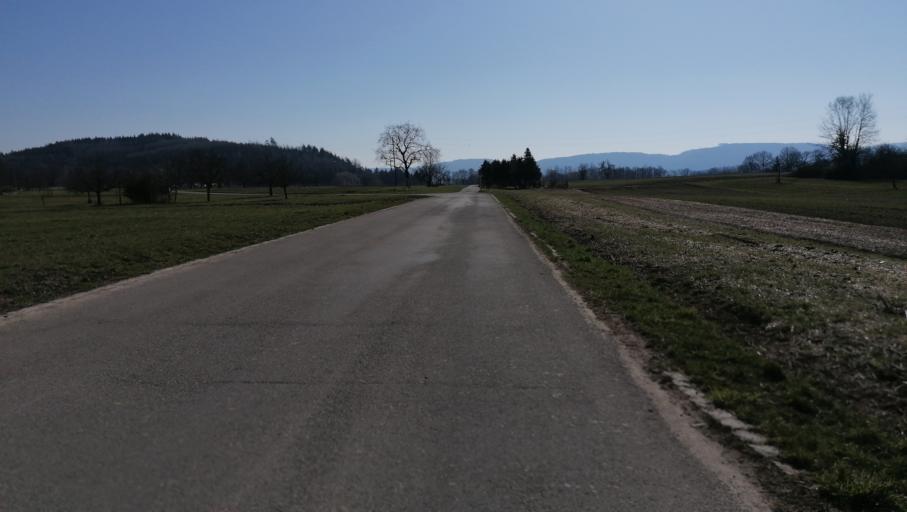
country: DE
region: Baden-Wuerttemberg
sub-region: Freiburg Region
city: Schworstadt
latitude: 47.5869
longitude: 7.9170
